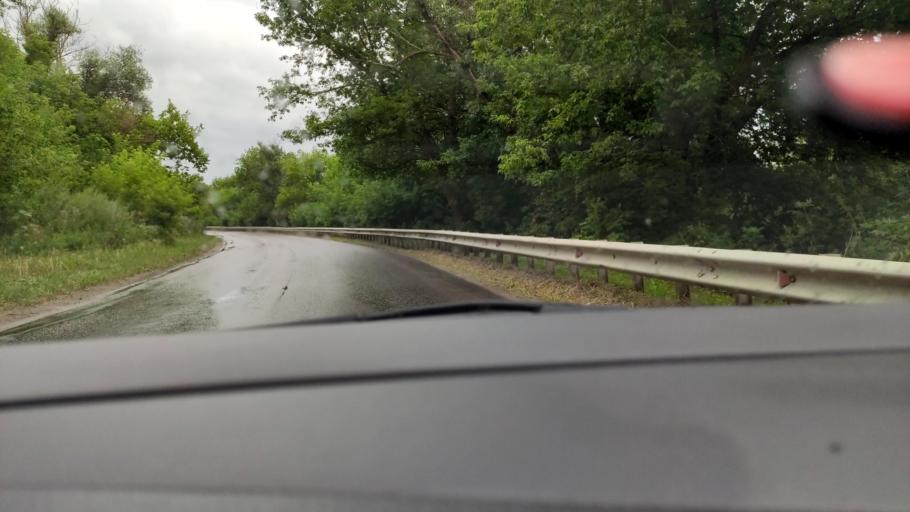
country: RU
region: Voronezj
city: Ramon'
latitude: 51.9026
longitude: 39.3423
